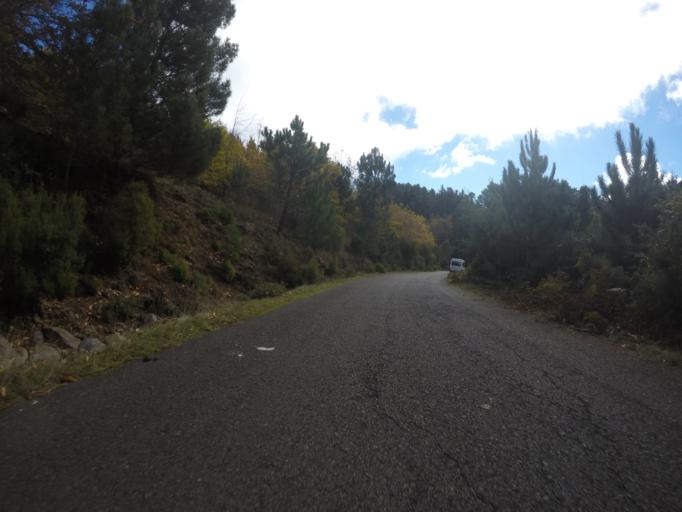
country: PT
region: Madeira
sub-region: Funchal
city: Nossa Senhora do Monte
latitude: 32.6994
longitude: -16.8849
